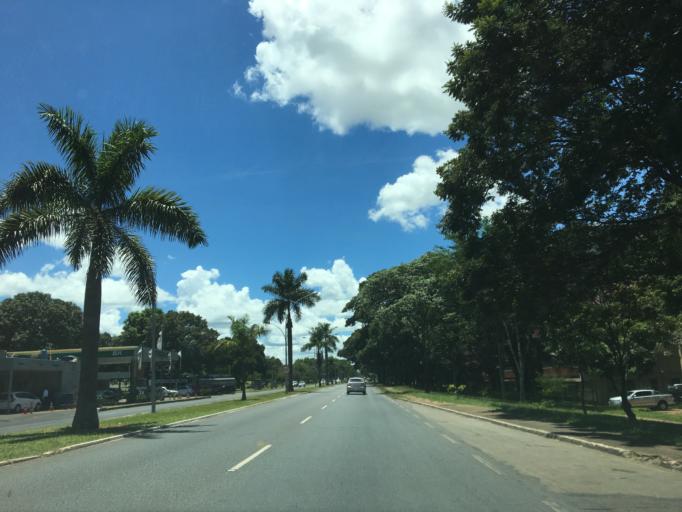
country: BR
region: Federal District
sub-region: Brasilia
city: Brasilia
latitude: -15.8313
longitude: -47.9194
